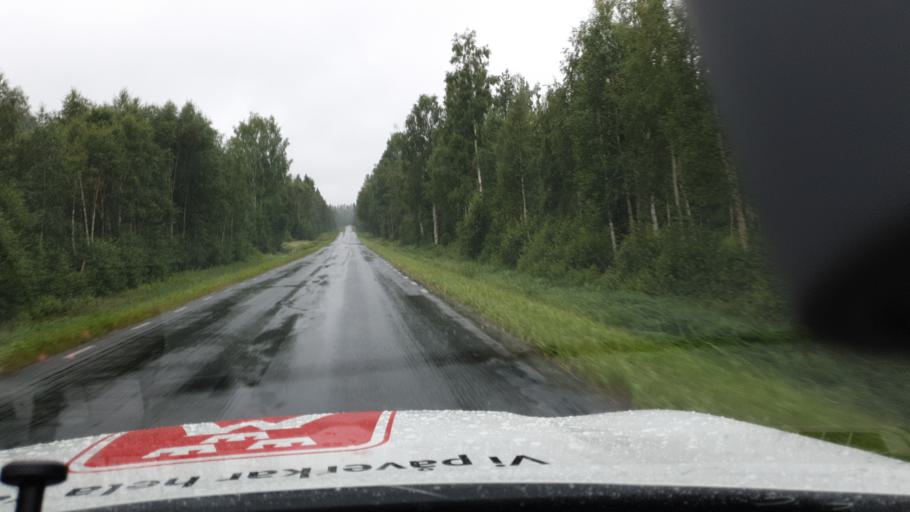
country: SE
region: Vaesterbotten
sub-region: Skelleftea Kommun
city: Burea
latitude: 64.6095
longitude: 21.1332
